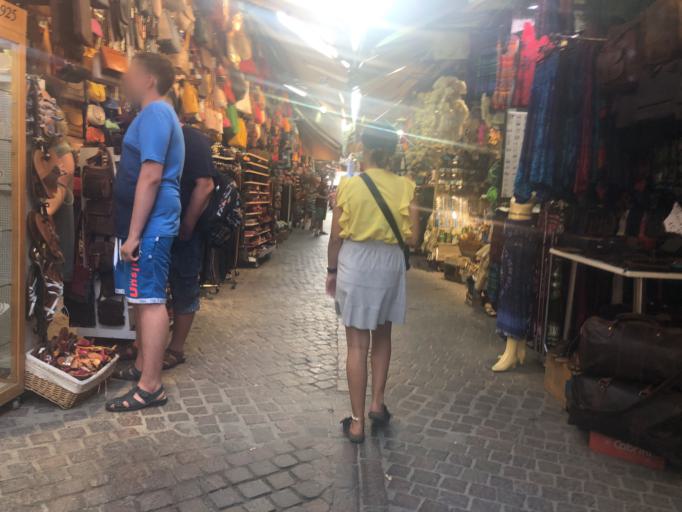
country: GR
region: Crete
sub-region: Nomos Chanias
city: Chania
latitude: 35.5147
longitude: 24.0185
